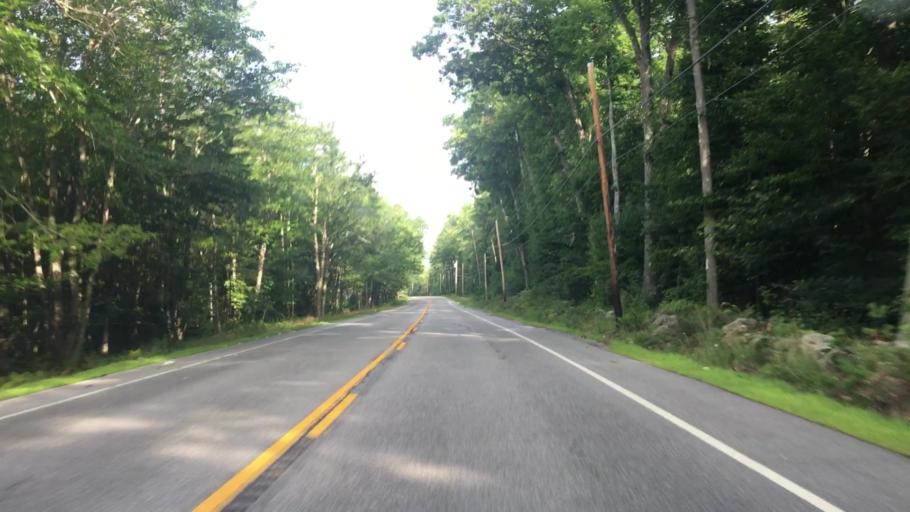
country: US
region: Maine
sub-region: York County
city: Limington
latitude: 43.7660
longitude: -70.7139
